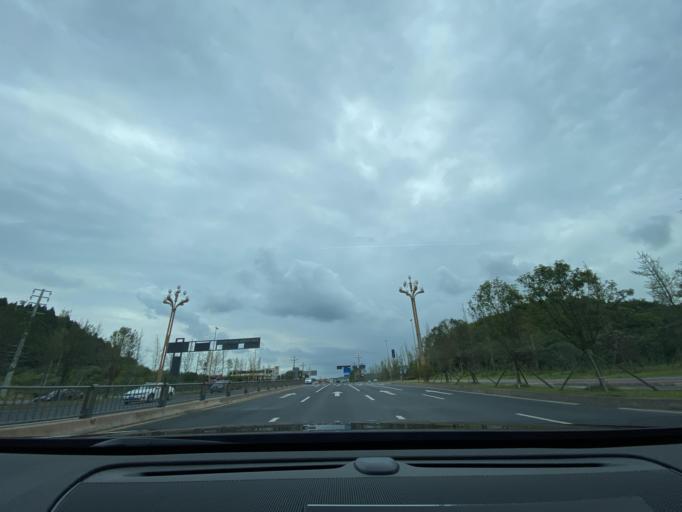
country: CN
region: Sichuan
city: Jiancheng
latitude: 30.4494
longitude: 104.4959
